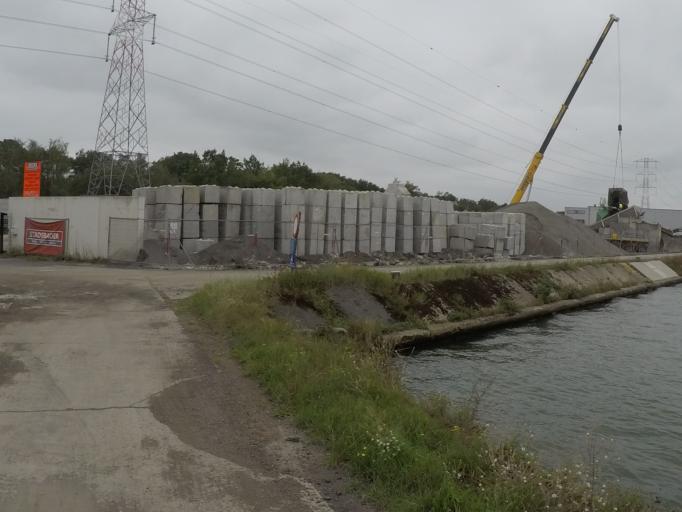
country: BE
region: Flanders
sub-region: Provincie Antwerpen
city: Grobbendonk
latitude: 51.1793
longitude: 4.7402
